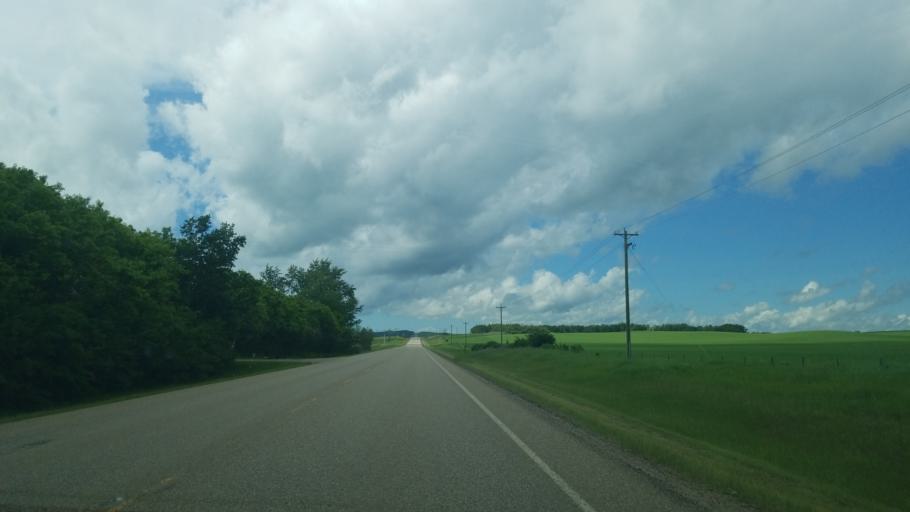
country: CA
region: Saskatchewan
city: Lloydminster
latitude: 53.1617
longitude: -110.1638
